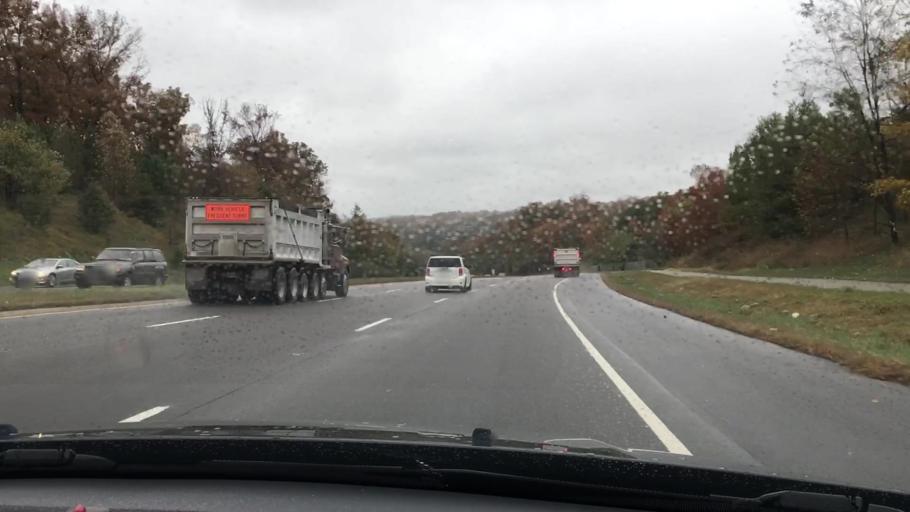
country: US
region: Virginia
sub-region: Fairfax County
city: Lorton
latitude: 38.6904
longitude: -77.2569
